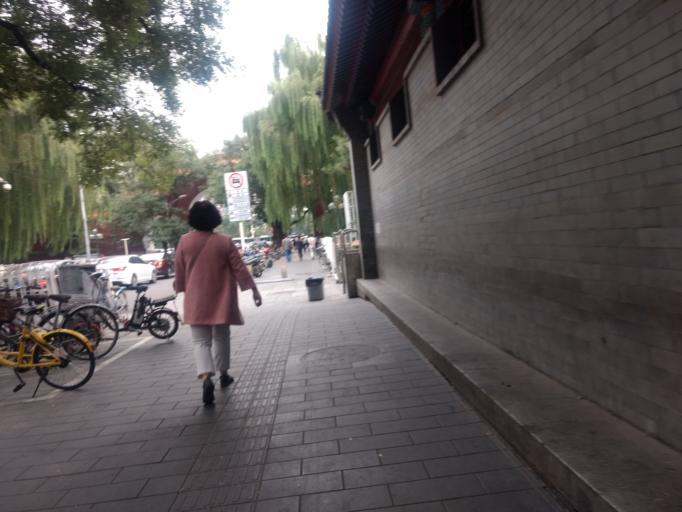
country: CN
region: Beijing
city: Beijing
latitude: 39.9076
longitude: 116.3969
